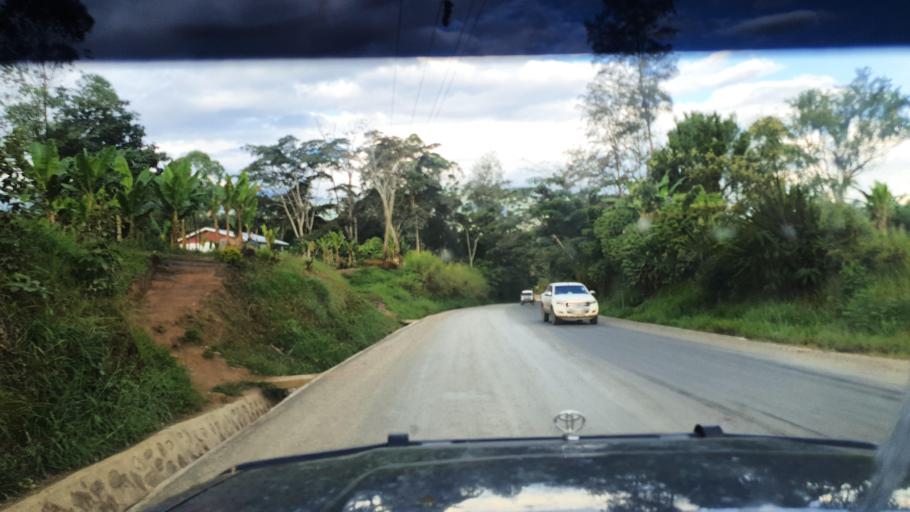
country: PG
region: Jiwaka
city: Minj
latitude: -5.9403
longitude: 144.8281
